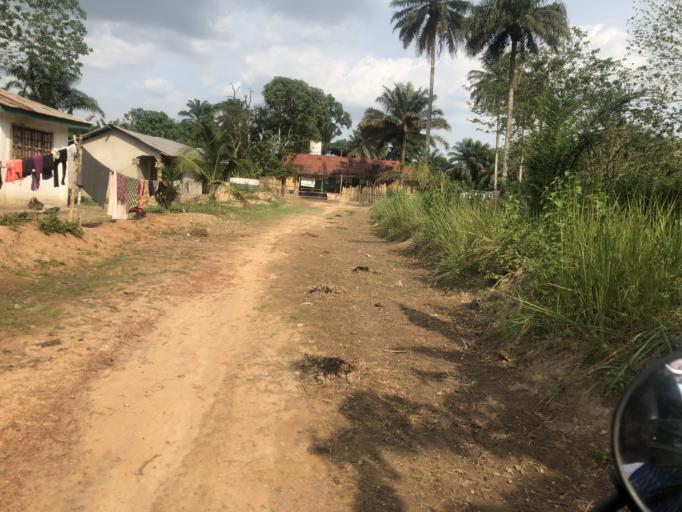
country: SL
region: Northern Province
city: Yonibana
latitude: 8.4398
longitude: -12.2441
